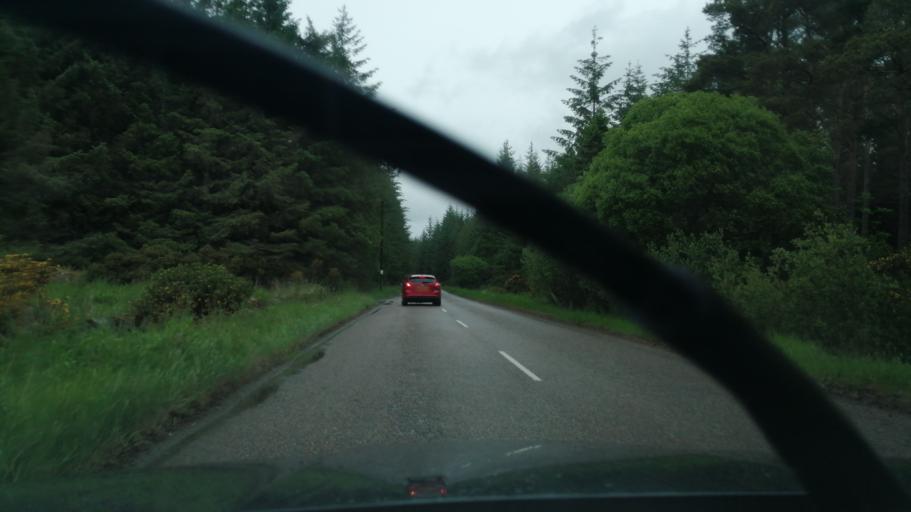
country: GB
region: Scotland
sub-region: Aberdeenshire
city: Portsoy
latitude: 57.6301
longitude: -2.7183
